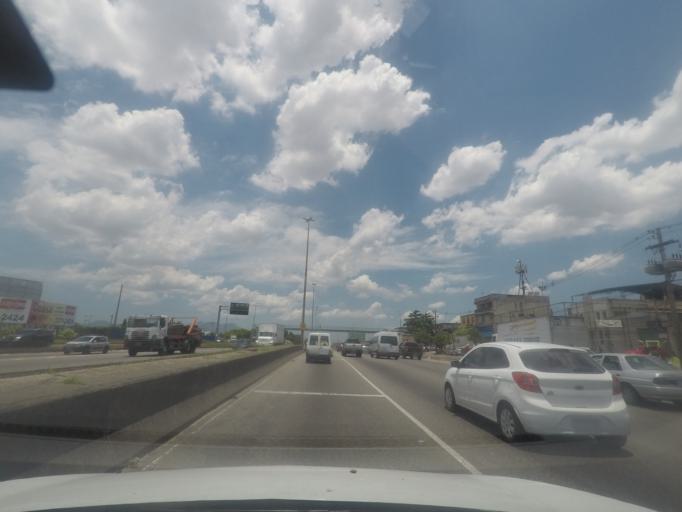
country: BR
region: Rio de Janeiro
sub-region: Sao Joao De Meriti
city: Sao Joao de Meriti
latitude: -22.8275
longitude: -43.3416
